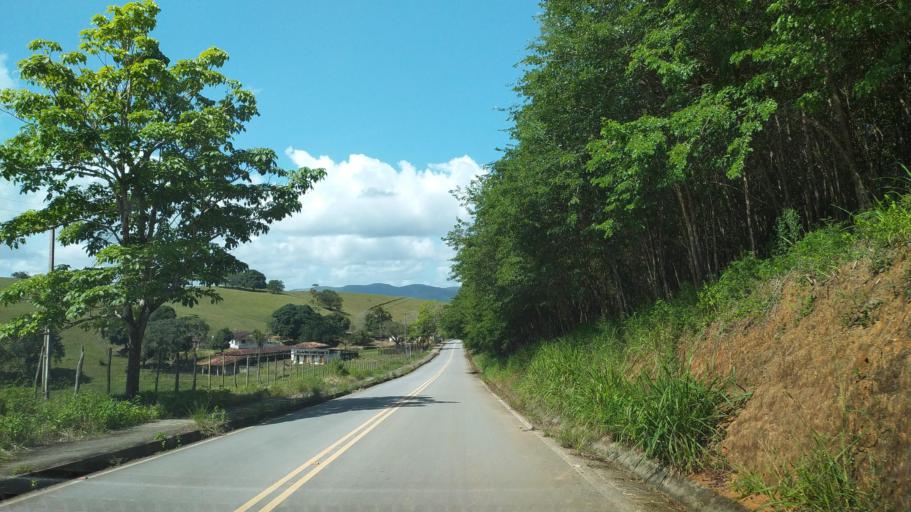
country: BR
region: Alagoas
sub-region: Uniao Dos Palmares
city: Uniao dos Palmares
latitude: -9.1623
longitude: -36.0708
